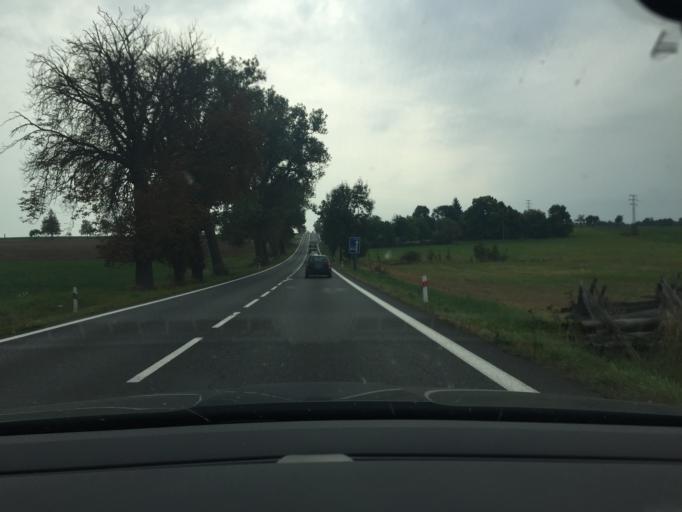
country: CZ
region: Central Bohemia
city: Milin
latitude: 49.6070
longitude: 14.0607
